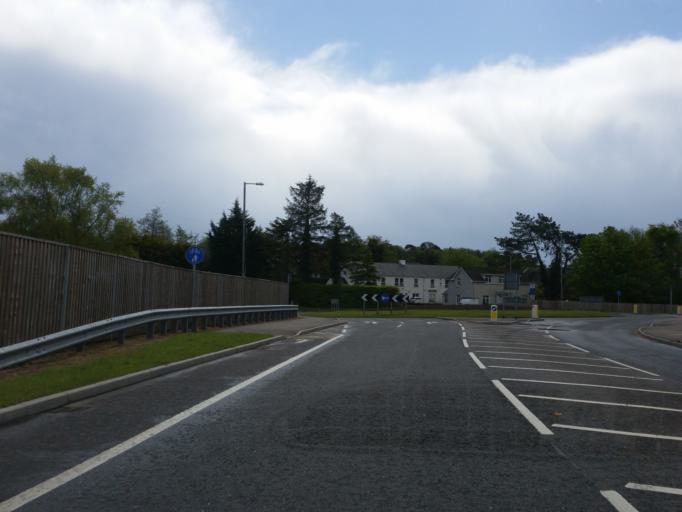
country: GB
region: Northern Ireland
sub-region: Fermanagh District
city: Enniskillen
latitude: 54.3495
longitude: -7.6162
